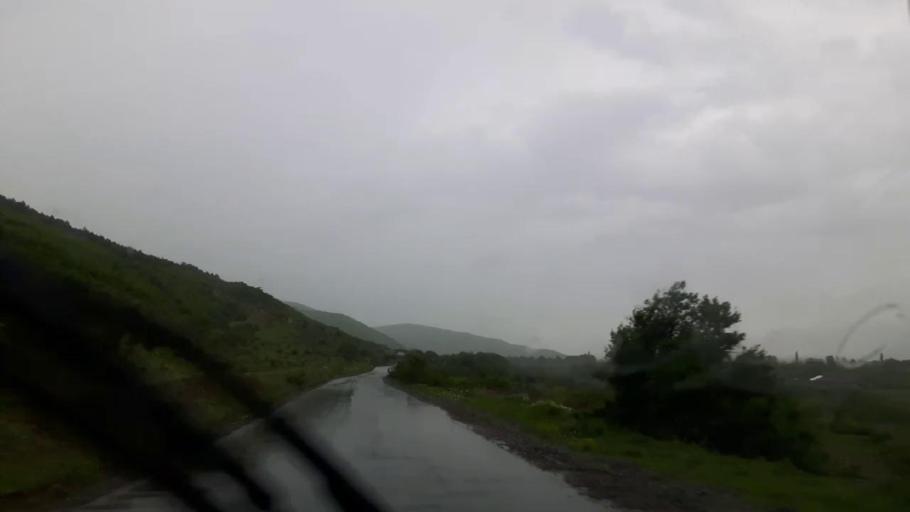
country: GE
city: Agara
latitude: 41.9837
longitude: 43.9284
